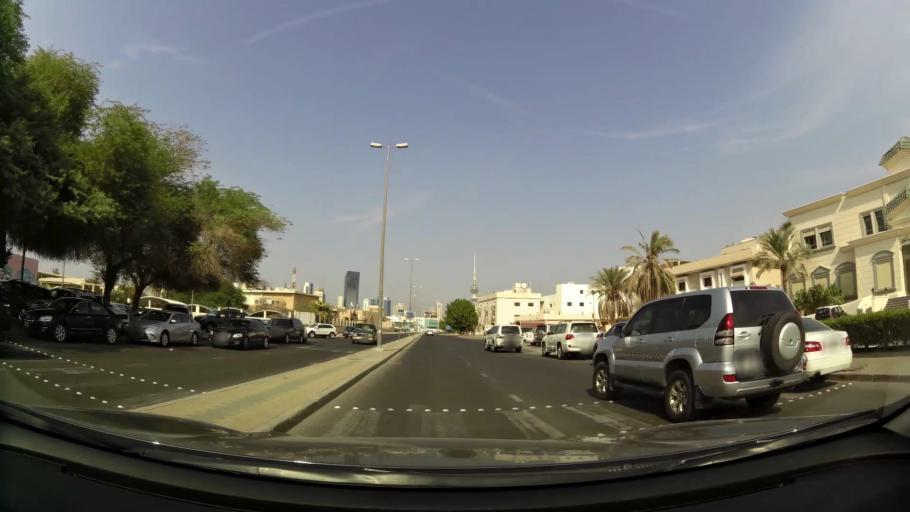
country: KW
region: Al Asimah
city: Ash Shamiyah
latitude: 29.3517
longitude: 47.9646
